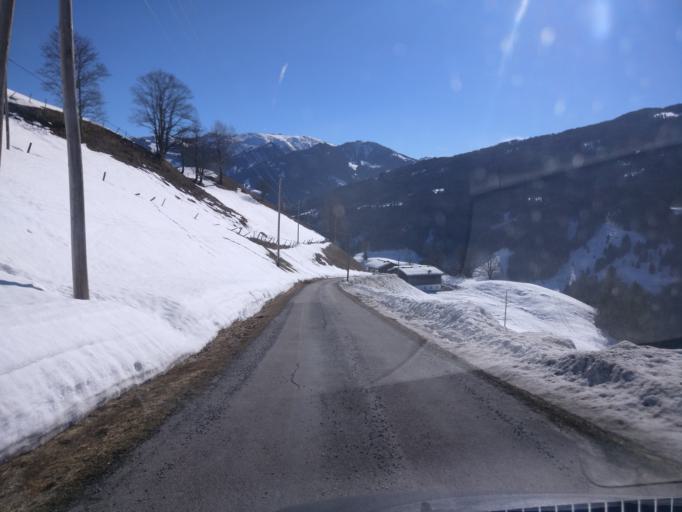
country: AT
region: Salzburg
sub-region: Politischer Bezirk Sankt Johann im Pongau
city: Wagrain
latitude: 47.3417
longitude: 13.2532
